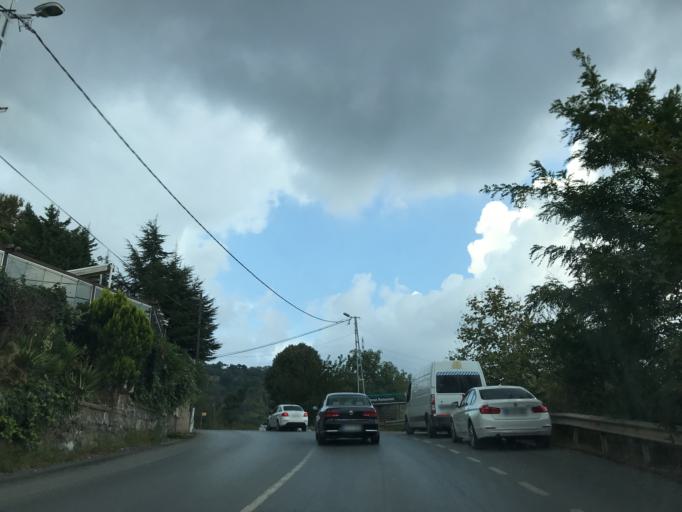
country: TR
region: Istanbul
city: Arikoey
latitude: 41.1801
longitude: 29.0466
